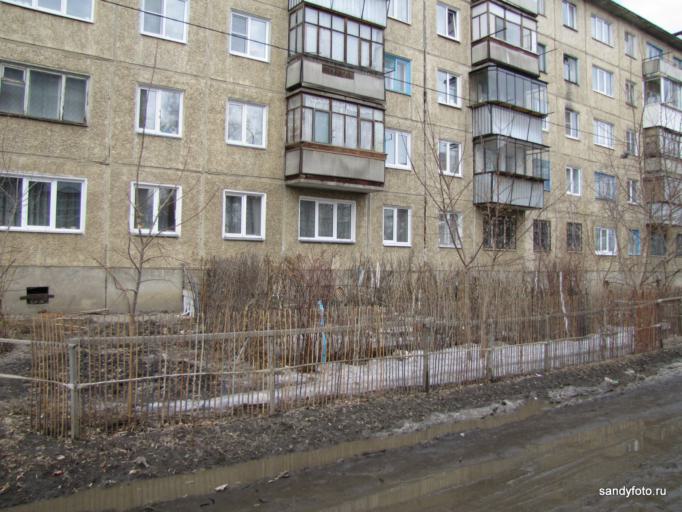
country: RU
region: Chelyabinsk
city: Troitsk
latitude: 54.1053
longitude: 61.5584
